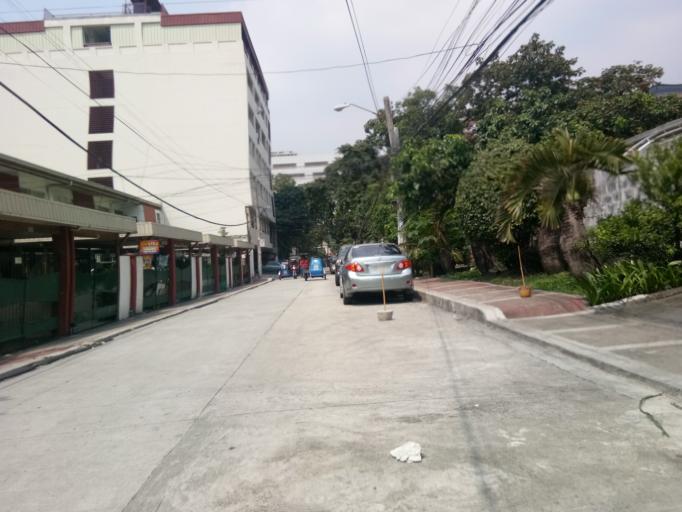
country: PH
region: Metro Manila
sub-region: Pasig
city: Pasig City
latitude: 14.6159
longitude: 121.0579
